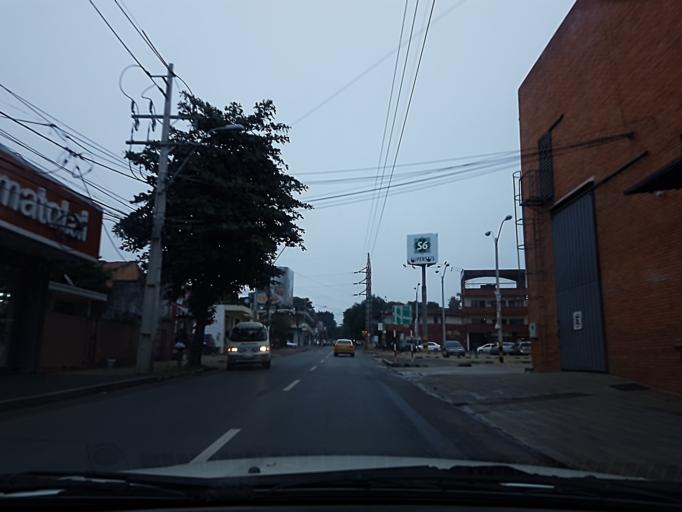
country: PY
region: Central
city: Fernando de la Mora
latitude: -25.2929
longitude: -57.5592
